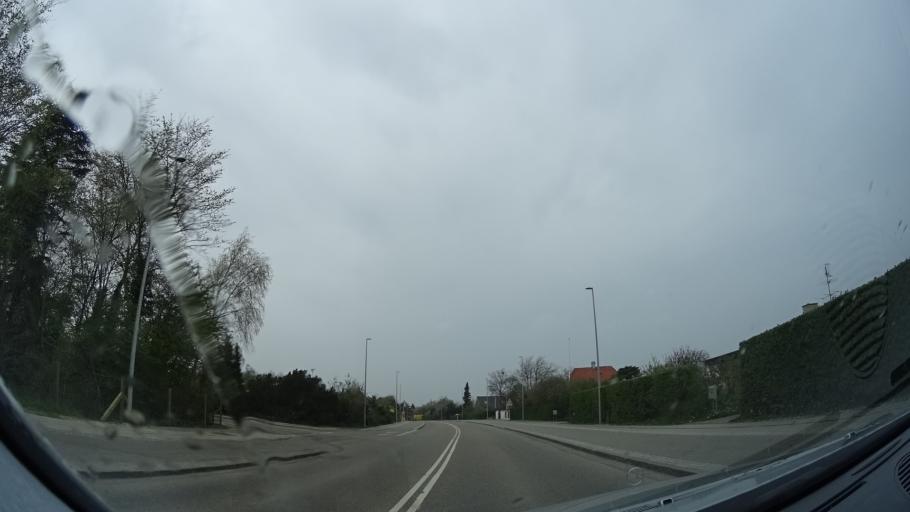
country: DK
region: Zealand
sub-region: Holbaek Kommune
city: Holbaek
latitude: 55.7138
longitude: 11.7438
